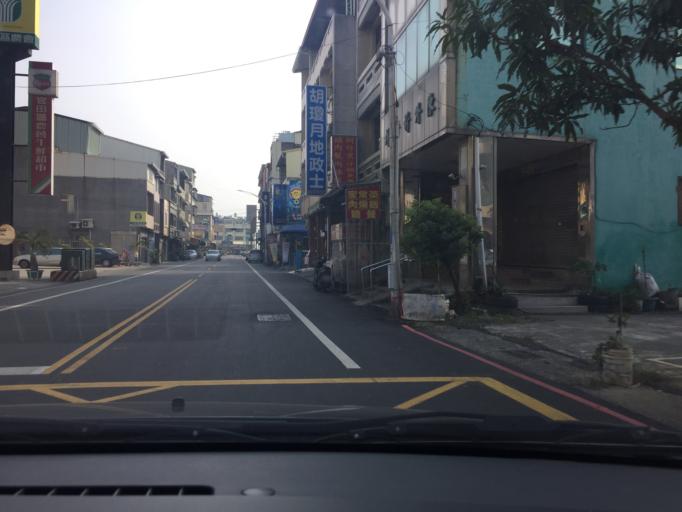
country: TW
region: Taiwan
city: Xinying
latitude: 23.1940
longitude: 120.3183
